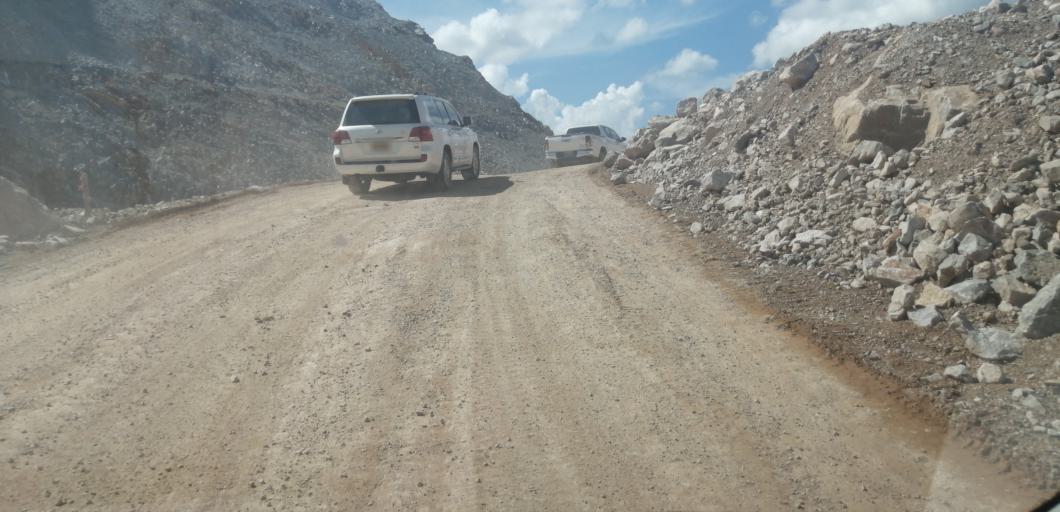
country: LA
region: Vientiane
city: Vangviang
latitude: 18.8699
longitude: 102.4280
